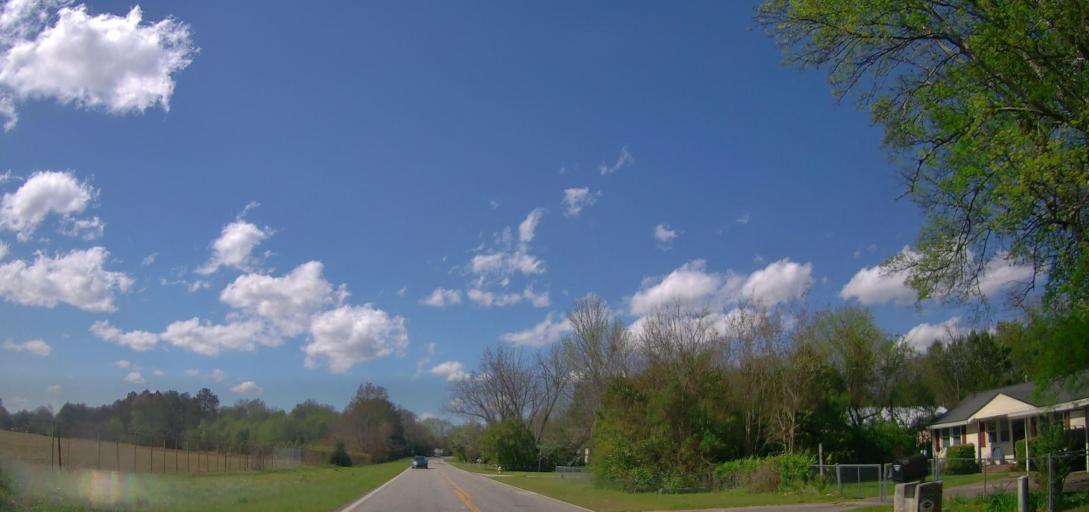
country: US
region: Georgia
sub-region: Bibb County
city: Macon
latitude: 32.8270
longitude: -83.5599
